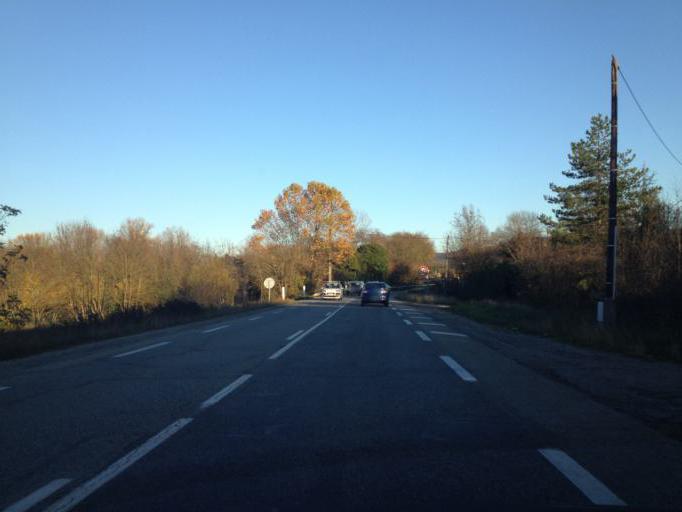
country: FR
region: Rhone-Alpes
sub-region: Departement de l'Ardeche
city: Chomerac
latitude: 44.7092
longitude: 4.6802
